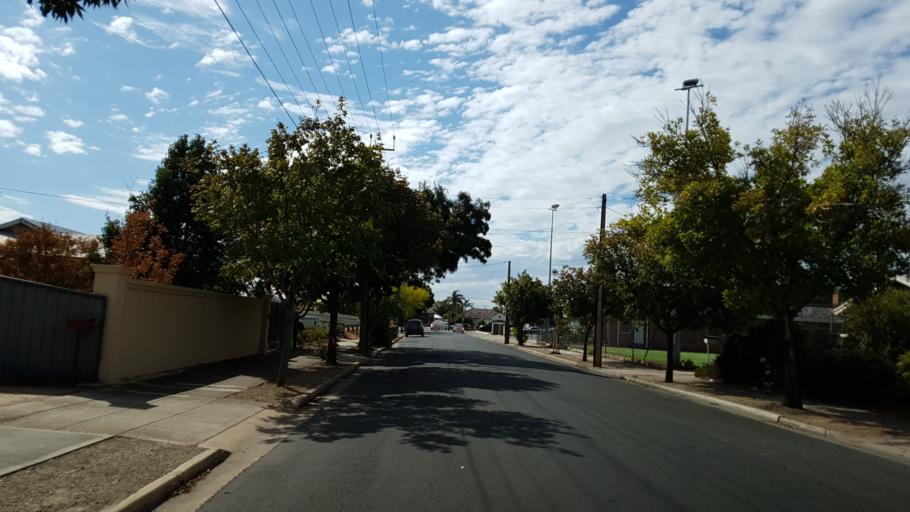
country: AU
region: South Australia
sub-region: City of West Torrens
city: Thebarton
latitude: -34.9263
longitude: 138.5485
